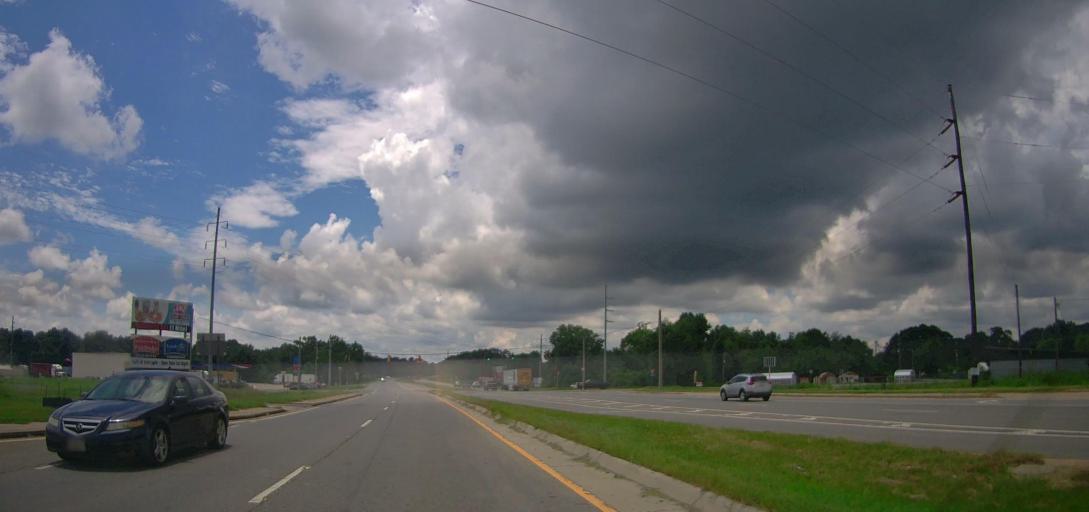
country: US
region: Georgia
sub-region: Pulaski County
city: Hawkinsville
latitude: 32.2821
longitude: -83.4507
